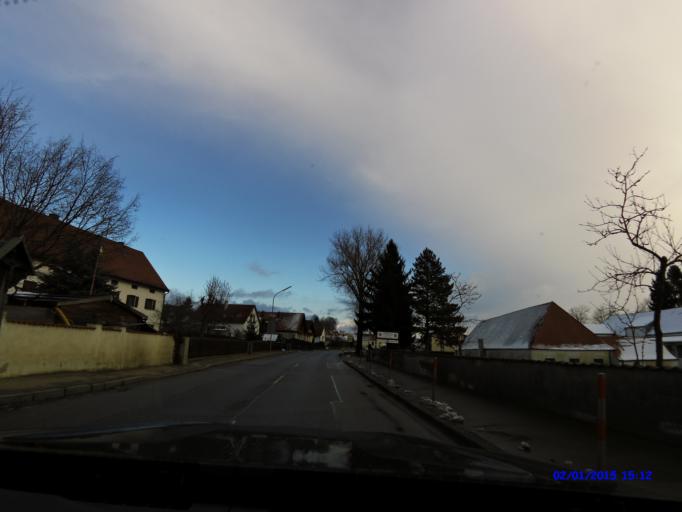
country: DE
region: Bavaria
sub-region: Lower Bavaria
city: Mainburg
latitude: 48.6269
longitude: 11.7958
